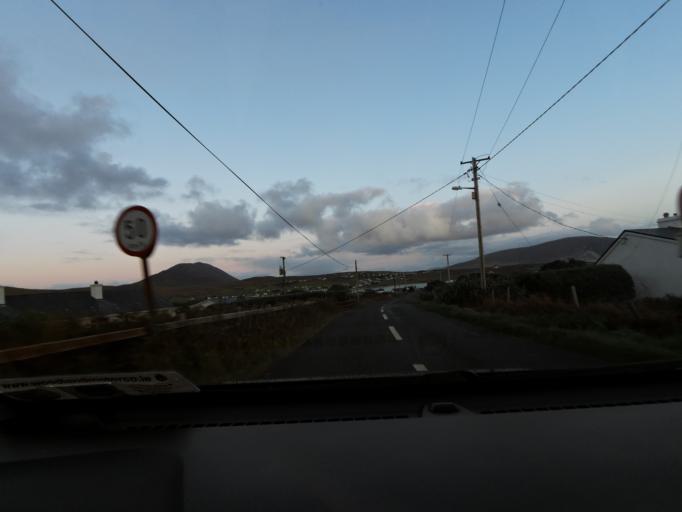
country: IE
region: Connaught
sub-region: Maigh Eo
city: Belmullet
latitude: 53.9716
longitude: -10.1424
